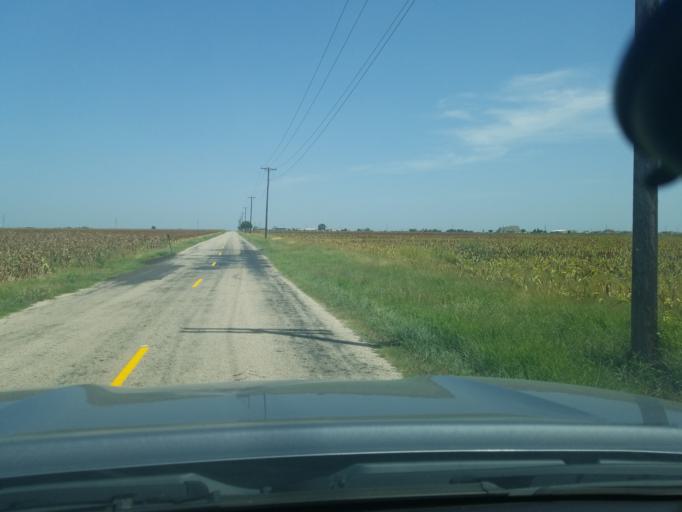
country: US
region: Texas
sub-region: Guadalupe County
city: Lake Dunlap
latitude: 29.6858
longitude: -98.0342
